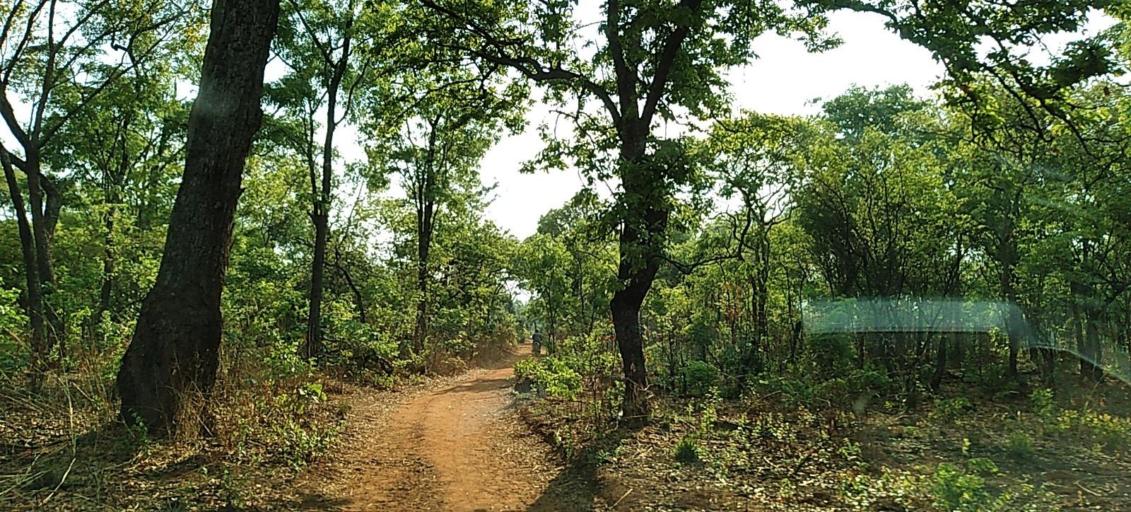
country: ZM
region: Copperbelt
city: Kalulushi
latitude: -12.9637
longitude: 27.7061
